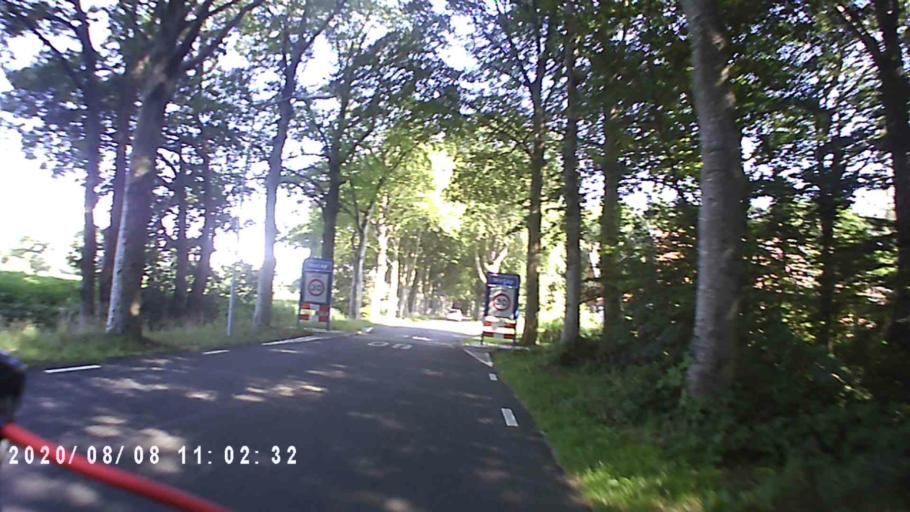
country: NL
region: Groningen
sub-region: Gemeente Leek
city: Leek
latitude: 53.1554
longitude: 6.3951
